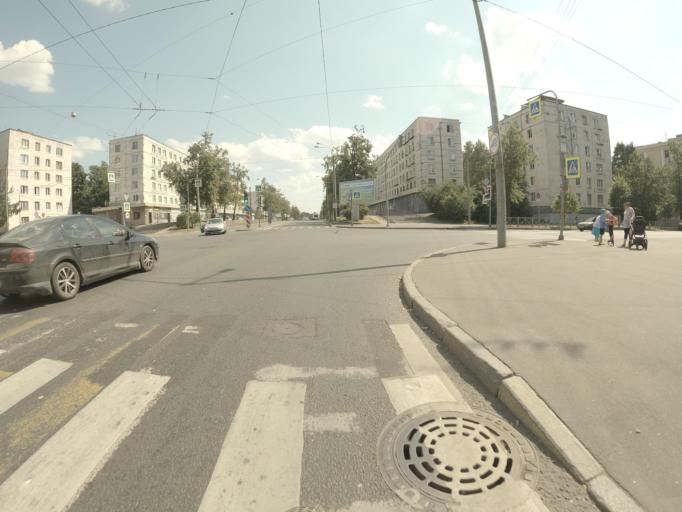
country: RU
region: St.-Petersburg
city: Avtovo
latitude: 59.8697
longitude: 30.2710
